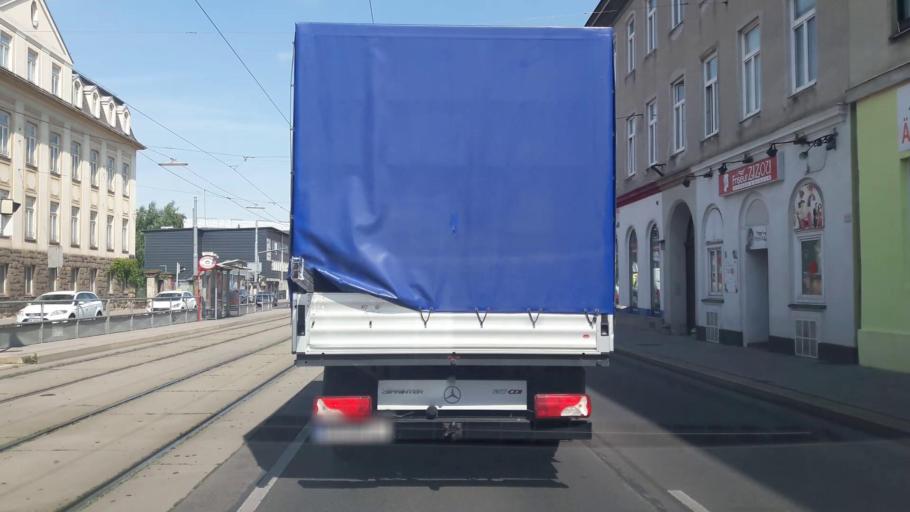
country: AT
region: Vienna
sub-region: Wien Stadt
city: Vienna
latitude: 48.1815
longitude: 16.3738
